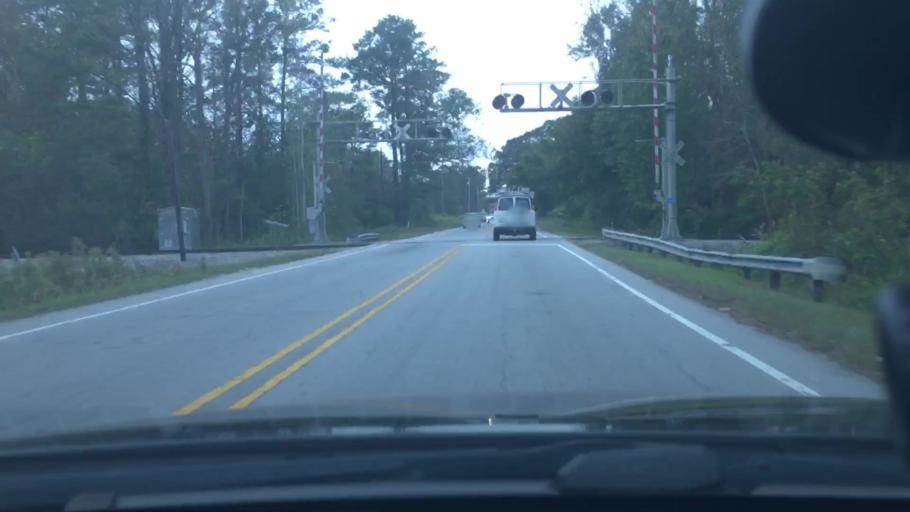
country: US
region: North Carolina
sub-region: Craven County
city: Vanceboro
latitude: 35.2379
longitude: -77.0759
